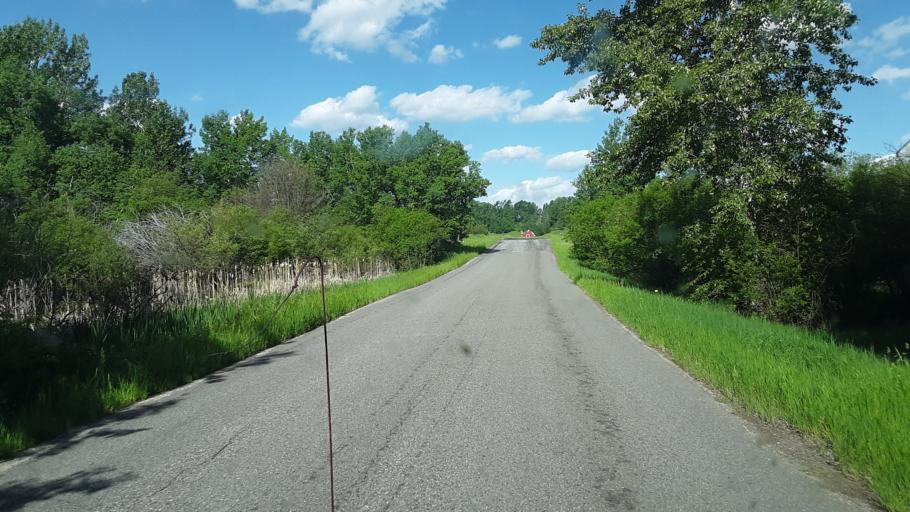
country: US
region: Montana
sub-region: Carbon County
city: Red Lodge
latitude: 45.2763
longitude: -109.2149
